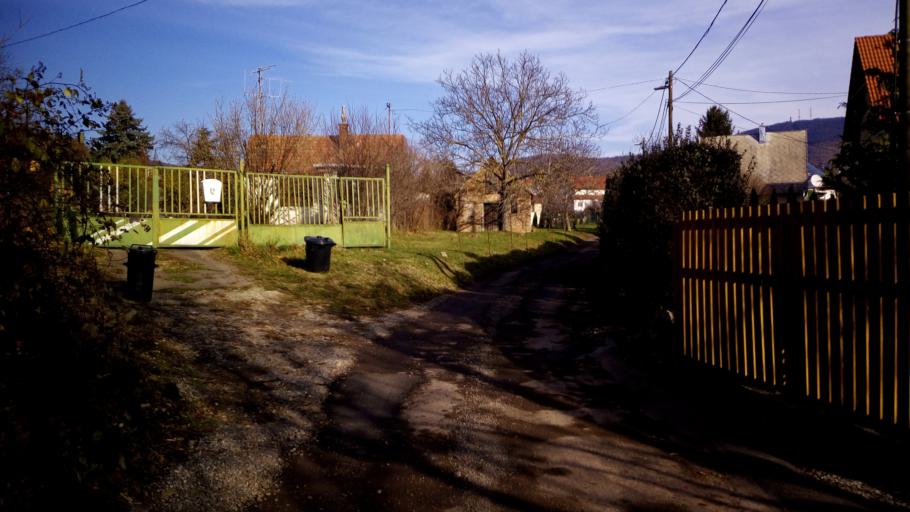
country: HU
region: Baranya
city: Pecs
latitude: 46.0893
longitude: 18.1827
